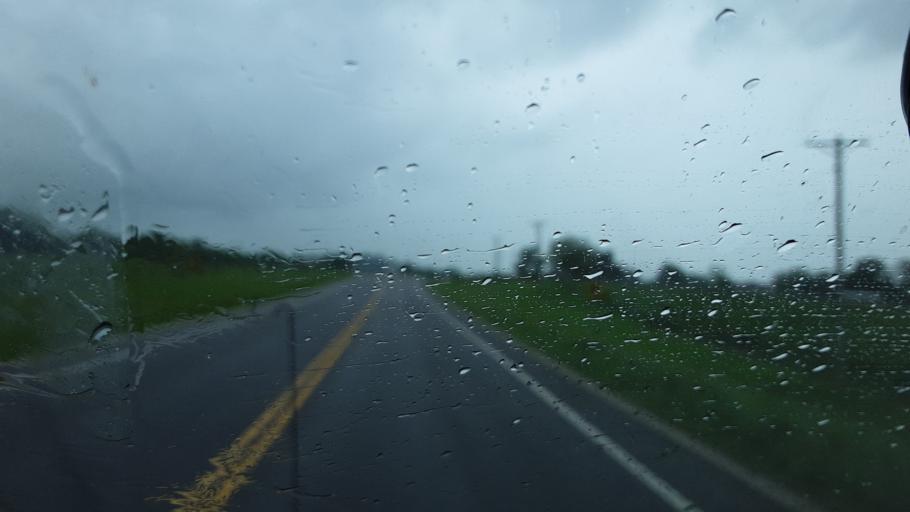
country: US
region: Missouri
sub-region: Monroe County
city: Paris
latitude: 39.4757
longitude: -92.2002
